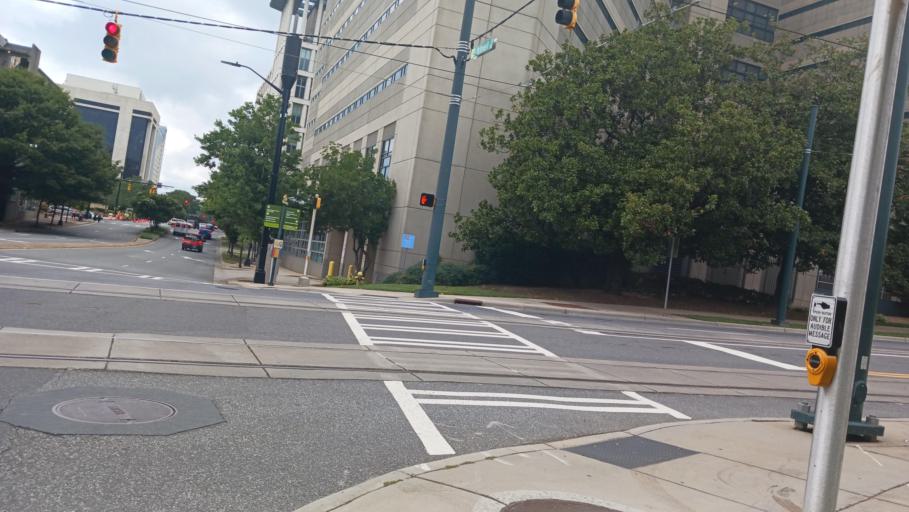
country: US
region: North Carolina
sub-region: Mecklenburg County
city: Charlotte
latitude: 35.2205
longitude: -80.8349
